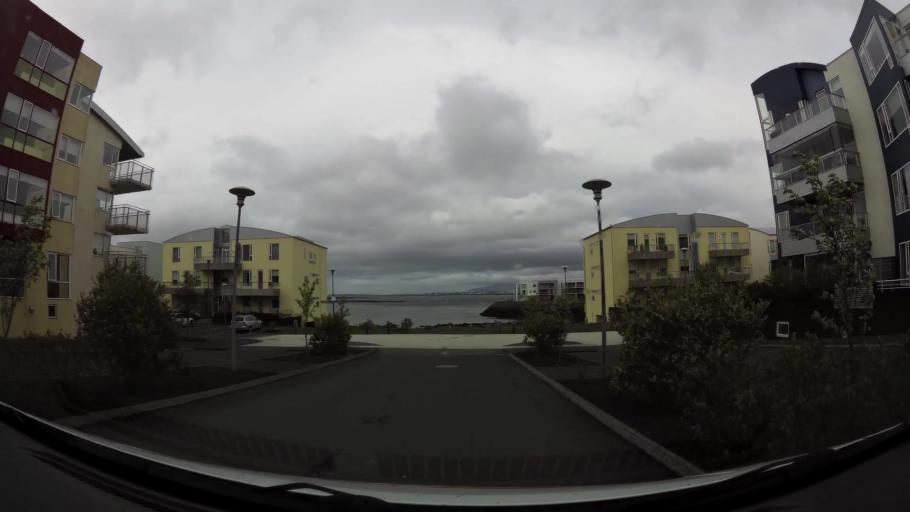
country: IS
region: Capital Region
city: Gardabaer
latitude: 64.0928
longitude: -21.9442
